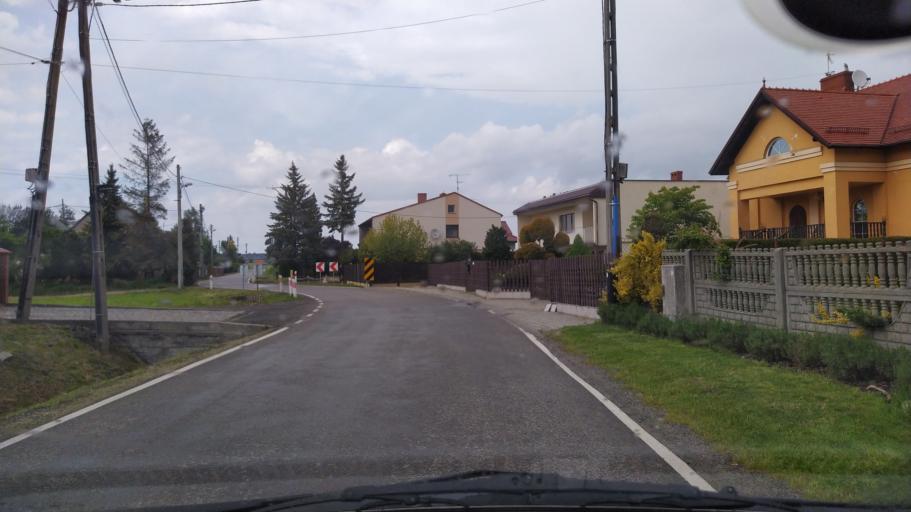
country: PL
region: Silesian Voivodeship
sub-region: Powiat gliwicki
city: Zernica
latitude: 50.2296
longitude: 18.6171
